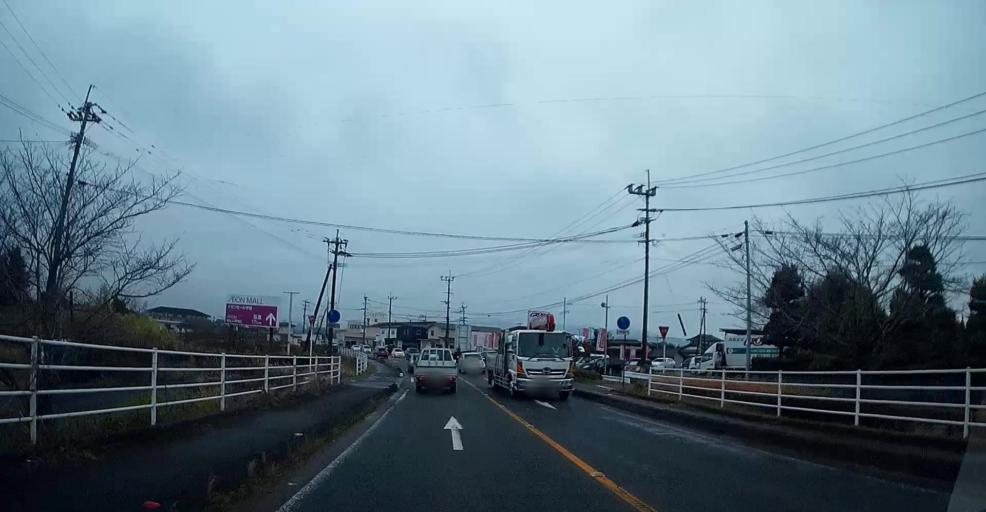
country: JP
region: Kumamoto
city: Uto
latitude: 32.7318
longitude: 130.7383
